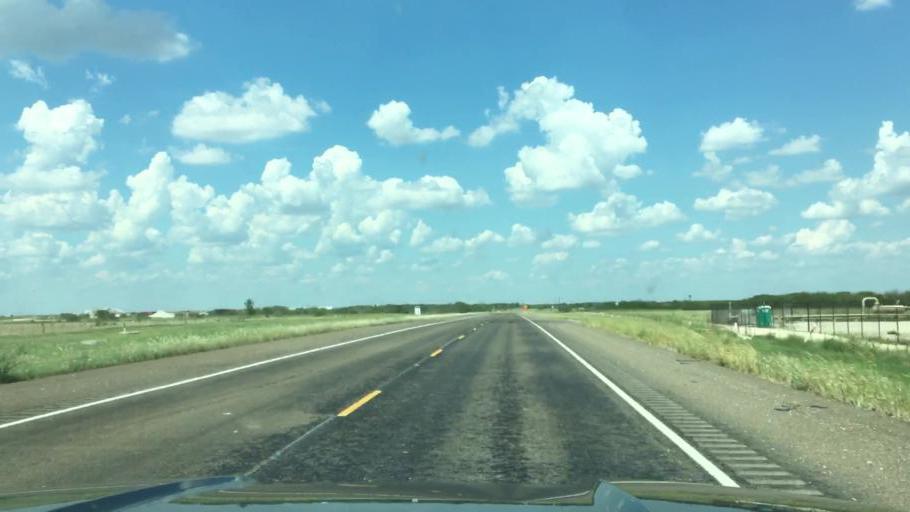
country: US
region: Texas
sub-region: Tarrant County
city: Haslet
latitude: 32.9988
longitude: -97.3424
